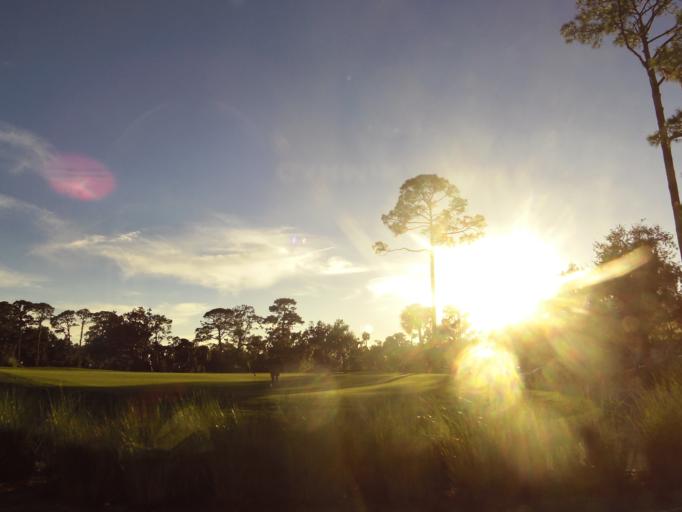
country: US
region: Florida
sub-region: Flagler County
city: Palm Coast
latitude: 29.5702
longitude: -81.1972
